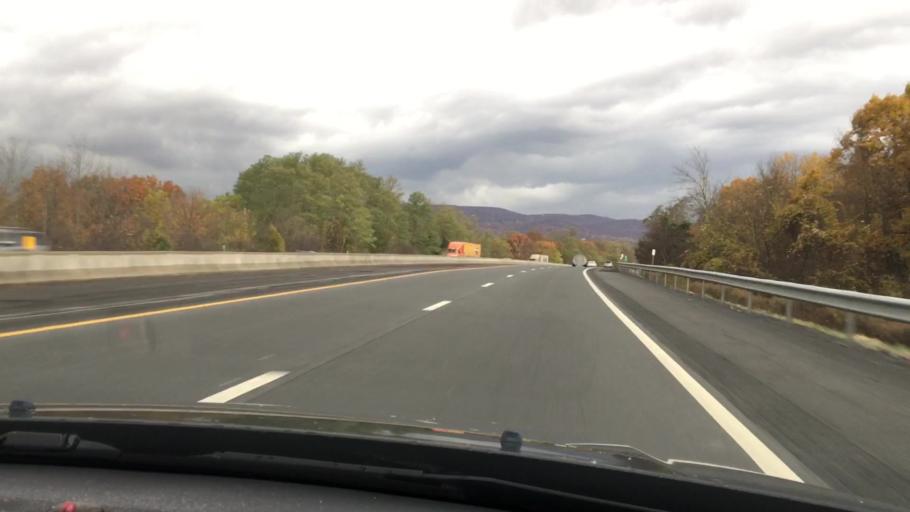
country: US
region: New York
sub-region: Orange County
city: Vails Gate
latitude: 41.4548
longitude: -74.0647
